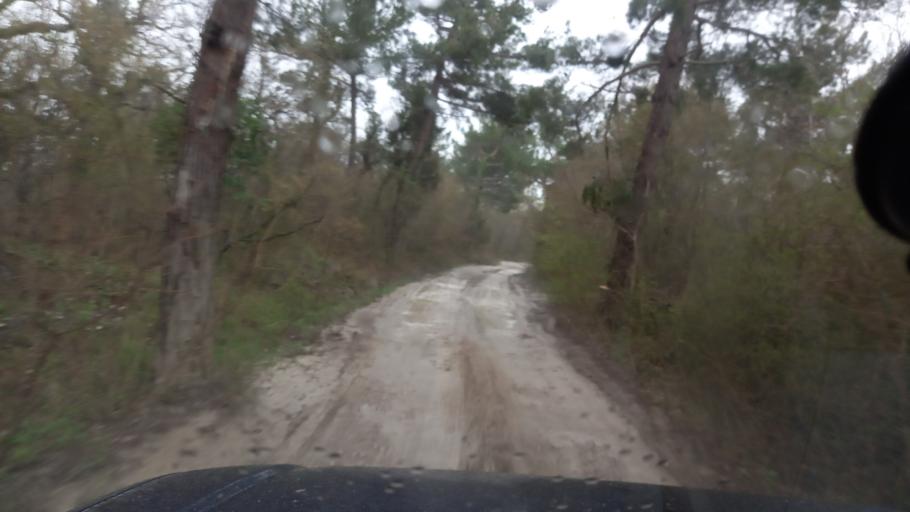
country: RU
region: Krasnodarskiy
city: Dzhubga
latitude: 44.3183
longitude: 38.6878
